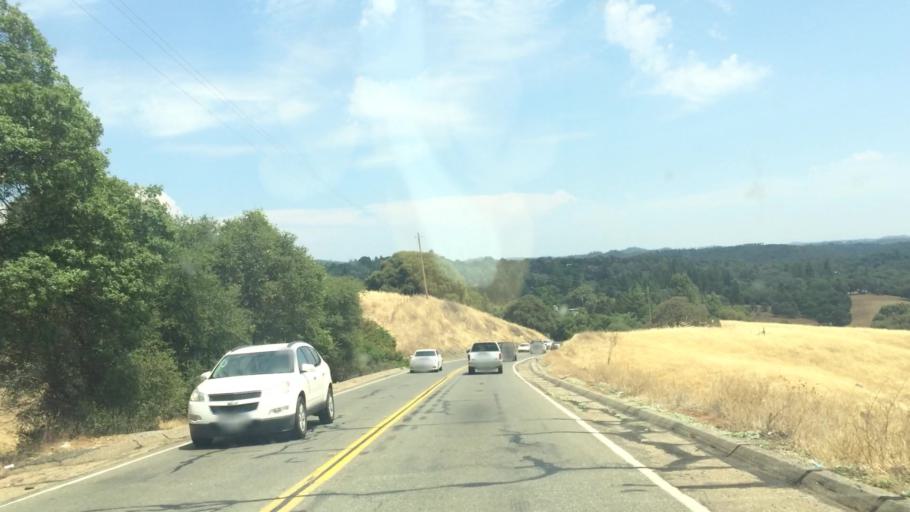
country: US
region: California
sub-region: Amador County
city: Sutter Creek
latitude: 38.4003
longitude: -120.7467
